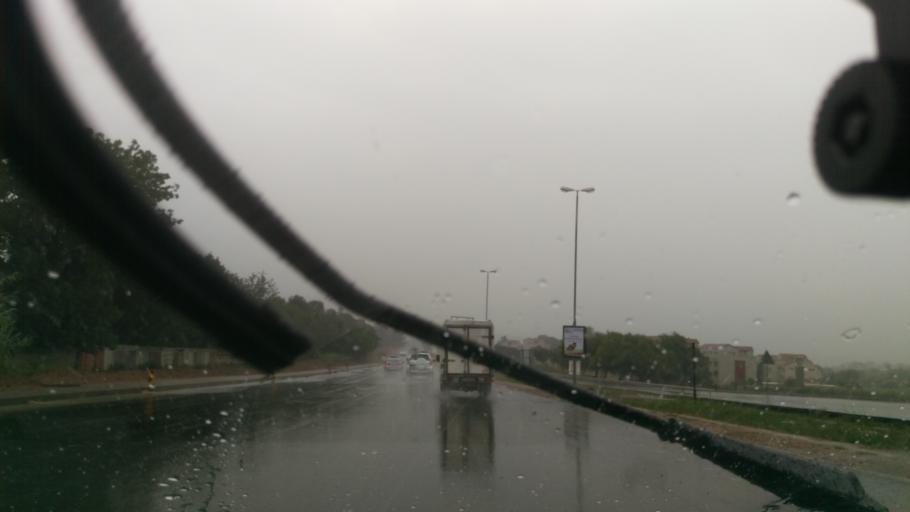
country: ZA
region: Gauteng
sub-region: City of Johannesburg Metropolitan Municipality
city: Diepsloot
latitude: -26.0216
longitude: 28.0026
